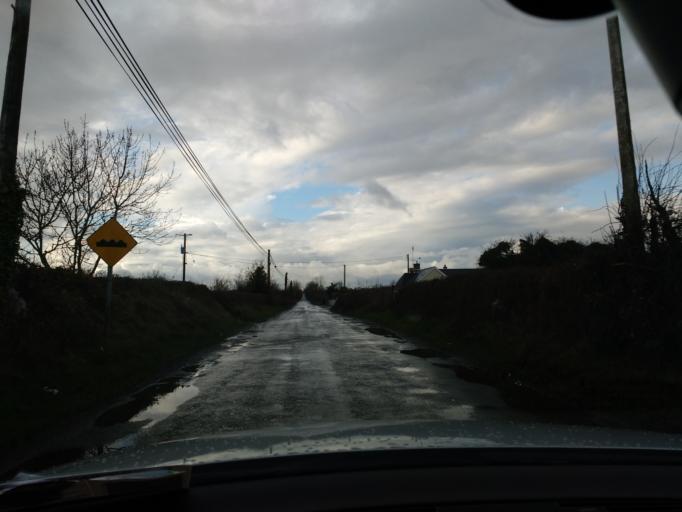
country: IE
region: Leinster
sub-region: Laois
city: Rathdowney
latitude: 52.6720
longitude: -7.5853
